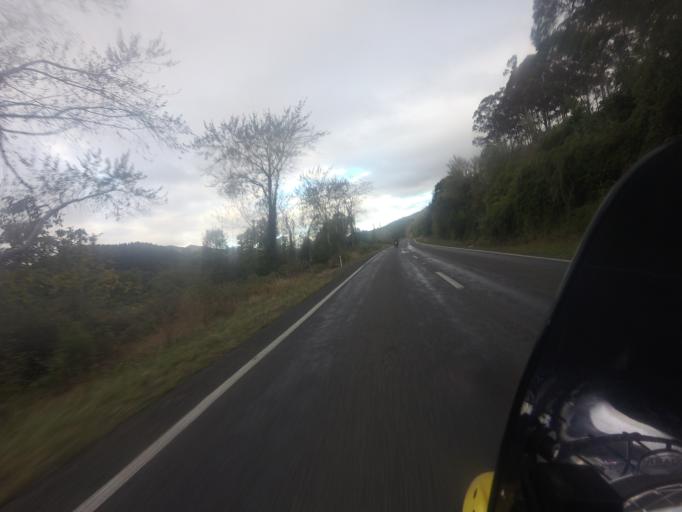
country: NZ
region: Gisborne
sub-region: Gisborne District
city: Gisborne
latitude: -38.4488
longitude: 177.6253
